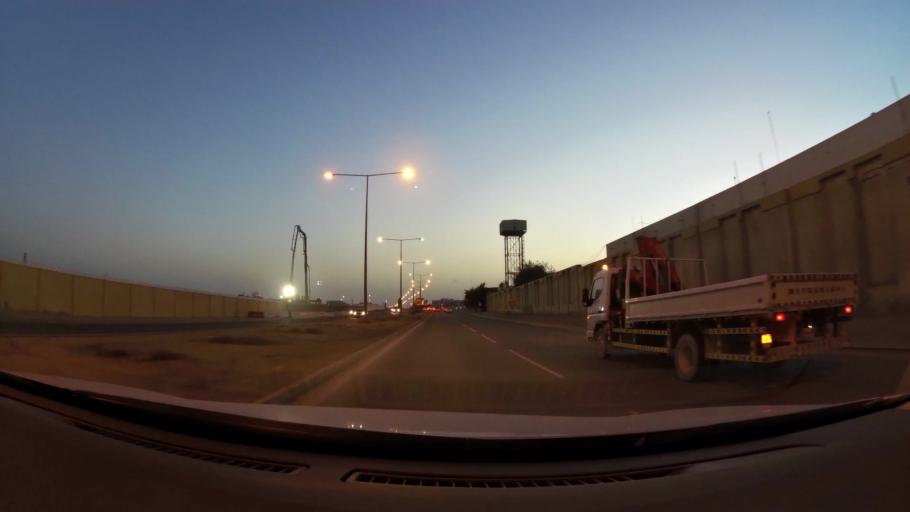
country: QA
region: Baladiyat ar Rayyan
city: Ar Rayyan
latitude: 25.3035
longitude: 51.4525
